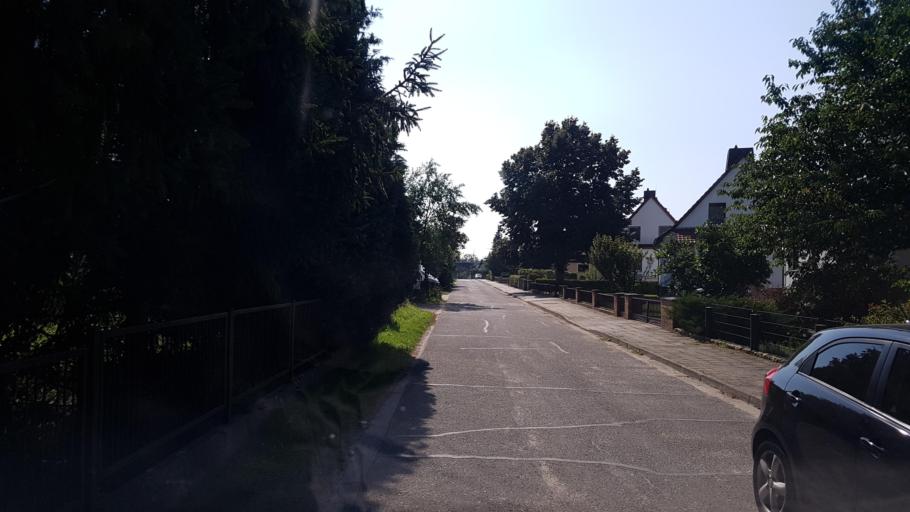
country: DE
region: Brandenburg
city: Vetschau
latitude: 51.7895
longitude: 14.0706
